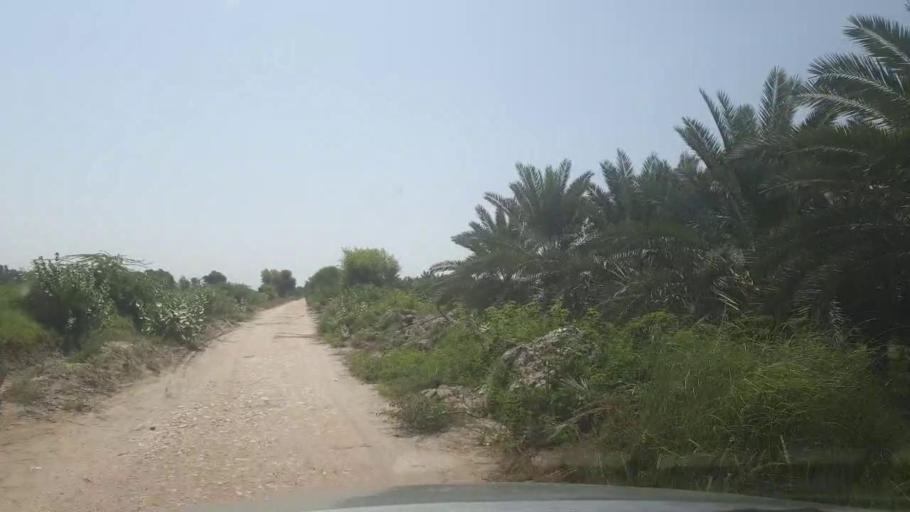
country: PK
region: Sindh
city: Khairpur
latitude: 27.3652
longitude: 69.0237
